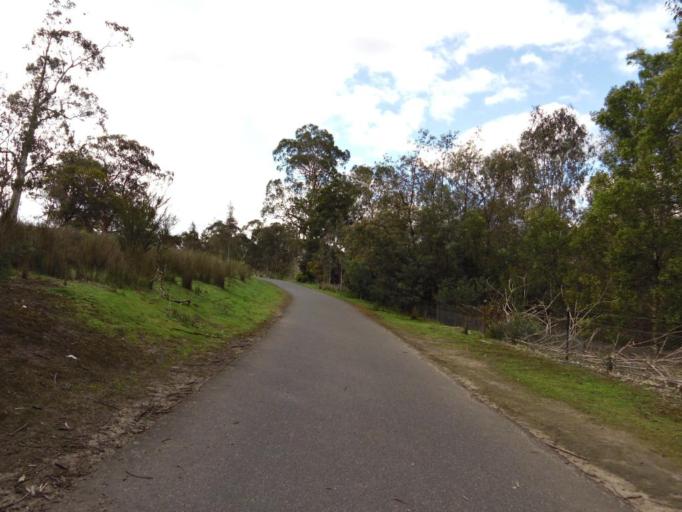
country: AU
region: Victoria
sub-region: Banyule
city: Darch
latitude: -37.7513
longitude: 145.1211
